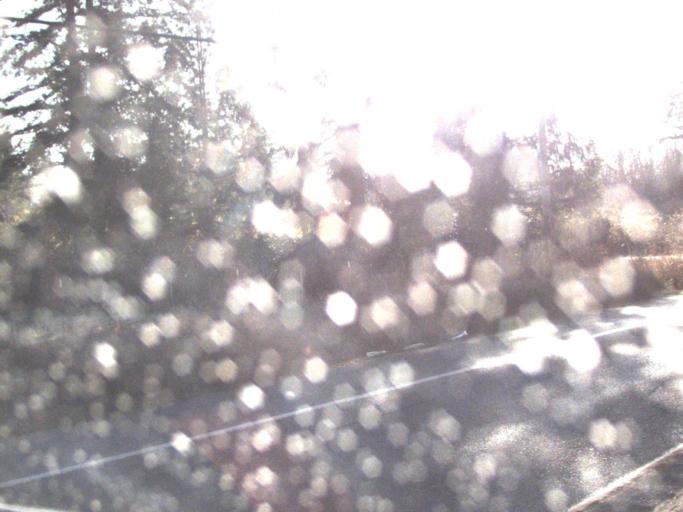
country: US
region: Washington
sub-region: Snohomish County
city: Arlington
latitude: 48.2179
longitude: -122.1084
